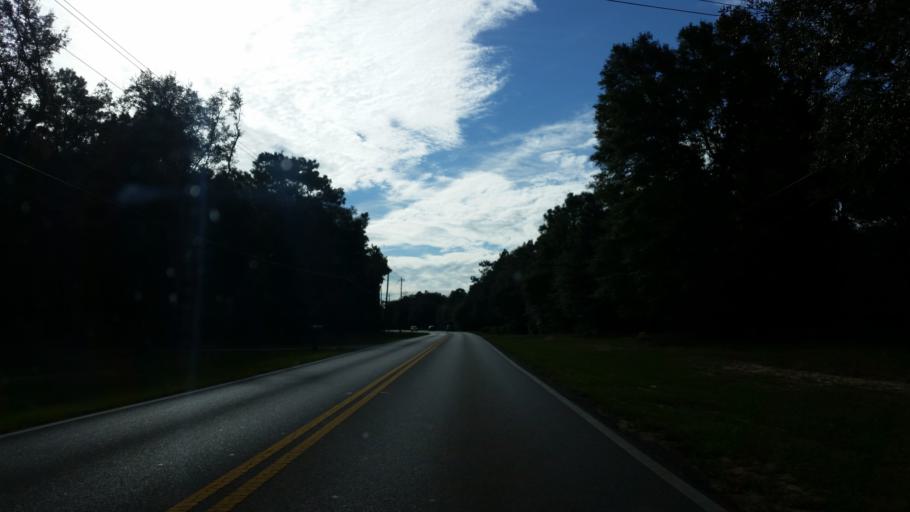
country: US
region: Florida
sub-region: Santa Rosa County
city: Milton
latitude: 30.6475
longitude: -87.0622
